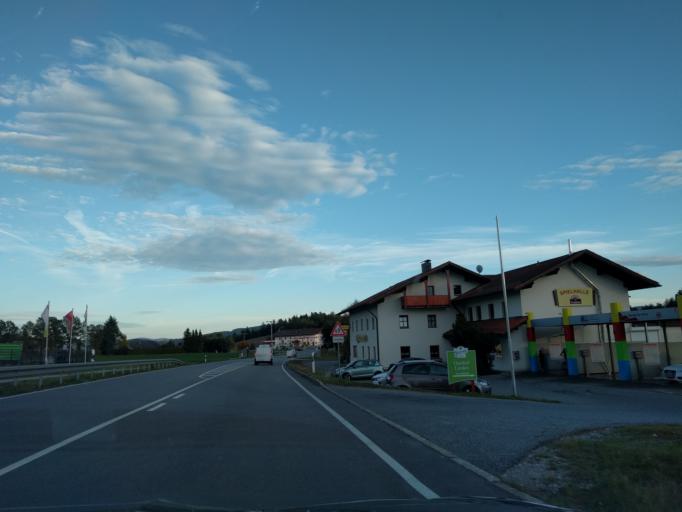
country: DE
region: Bavaria
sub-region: Lower Bavaria
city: Patersdorf
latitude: 49.0264
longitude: 12.9702
